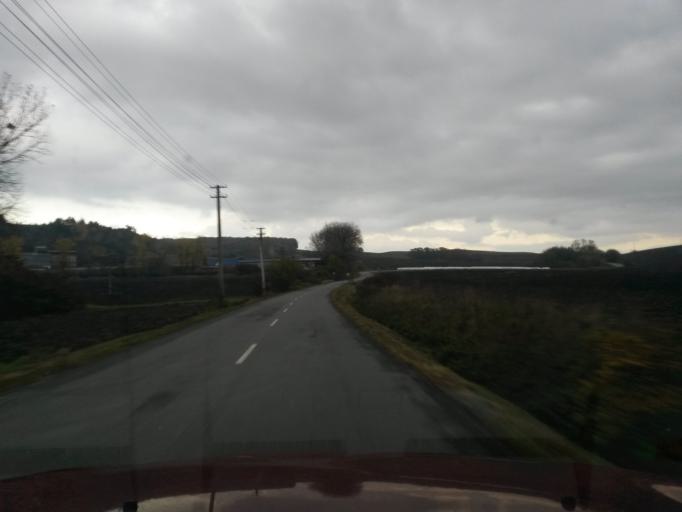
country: SK
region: Kosicky
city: Kosice
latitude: 48.8045
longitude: 21.2521
